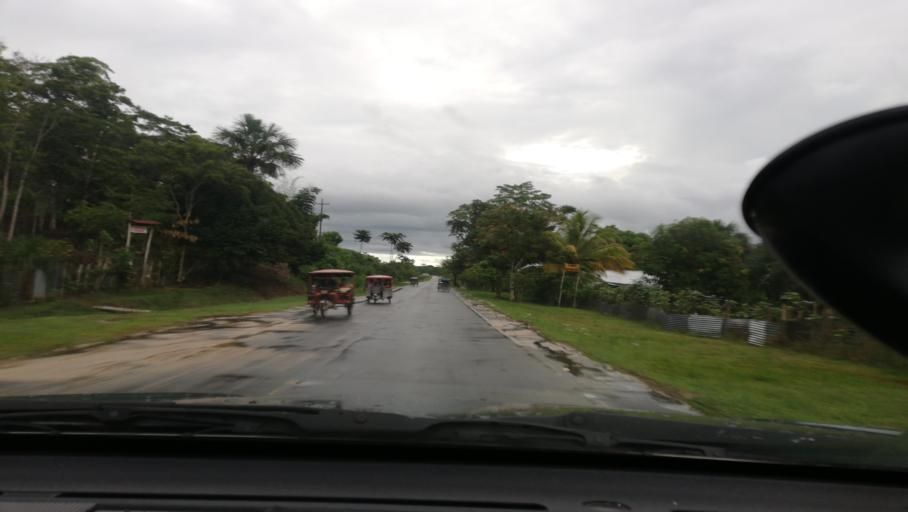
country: PE
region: Loreto
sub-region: Provincia de Maynas
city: Iquitos
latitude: -3.9067
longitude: -73.3600
